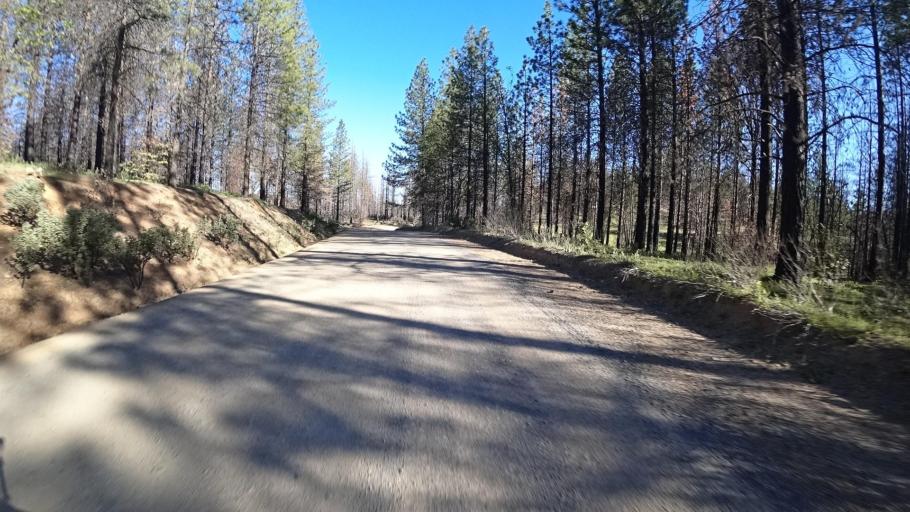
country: US
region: California
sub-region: Lake County
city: Upper Lake
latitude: 39.3317
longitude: -122.9566
